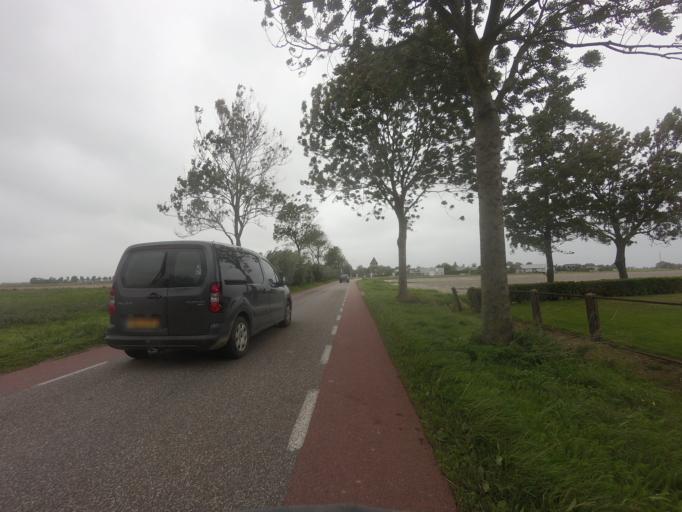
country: NL
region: Friesland
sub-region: Gemeente Ferwerderadiel
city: Ferwert
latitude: 53.3357
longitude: 5.8396
